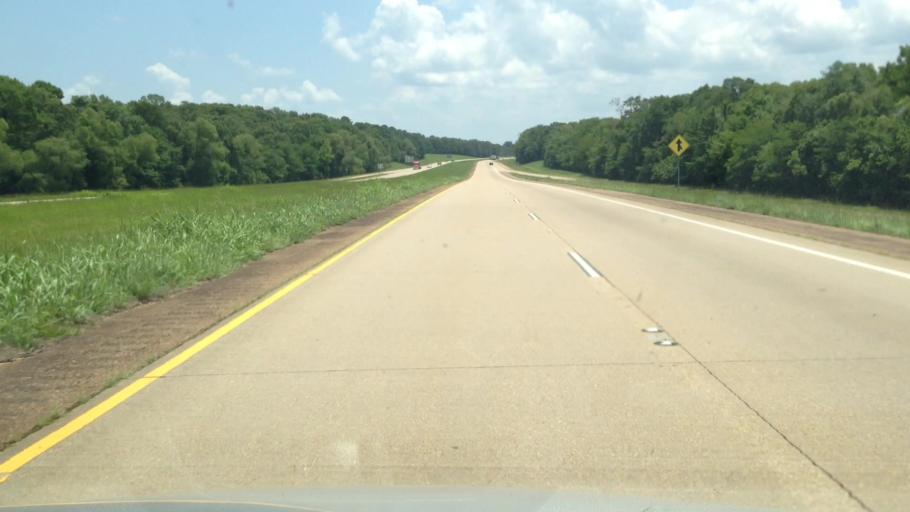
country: US
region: Louisiana
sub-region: Rapides Parish
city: Woodworth
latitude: 31.1622
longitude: -92.4586
